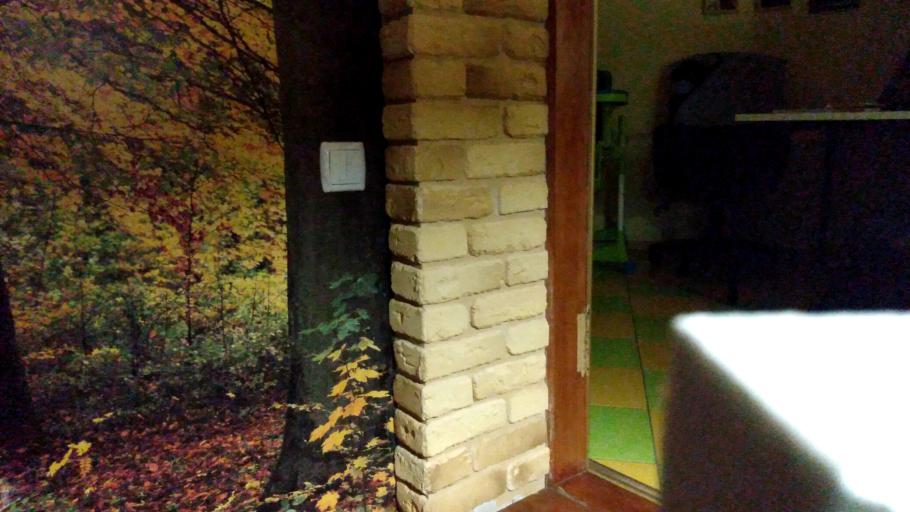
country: RU
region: Vologda
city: Lipin Bor
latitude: 60.8949
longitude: 37.9988
